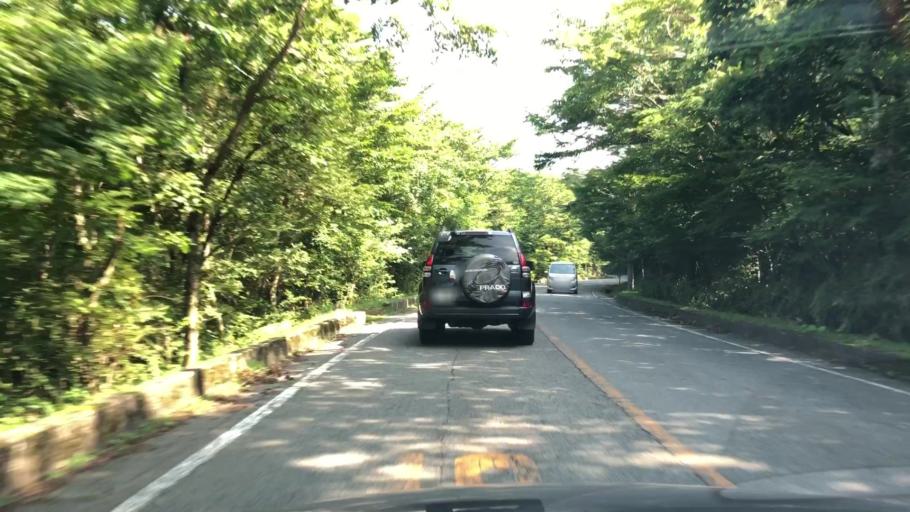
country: JP
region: Shizuoka
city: Gotemba
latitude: 35.3317
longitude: 138.8101
